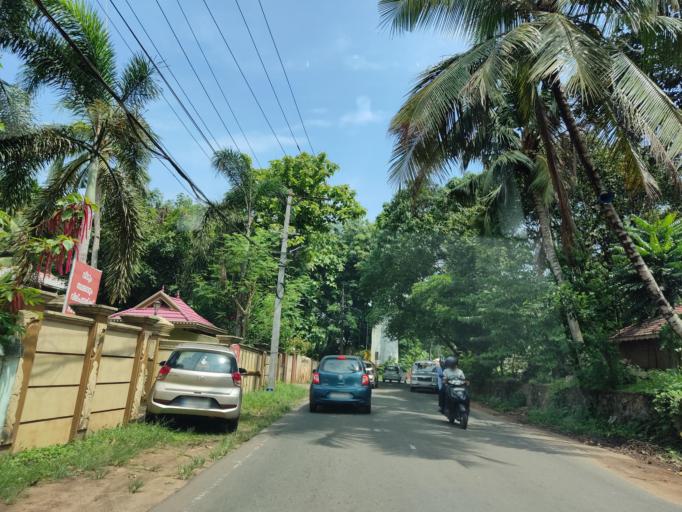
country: IN
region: Kerala
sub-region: Alappuzha
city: Chengannur
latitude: 9.3050
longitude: 76.5885
